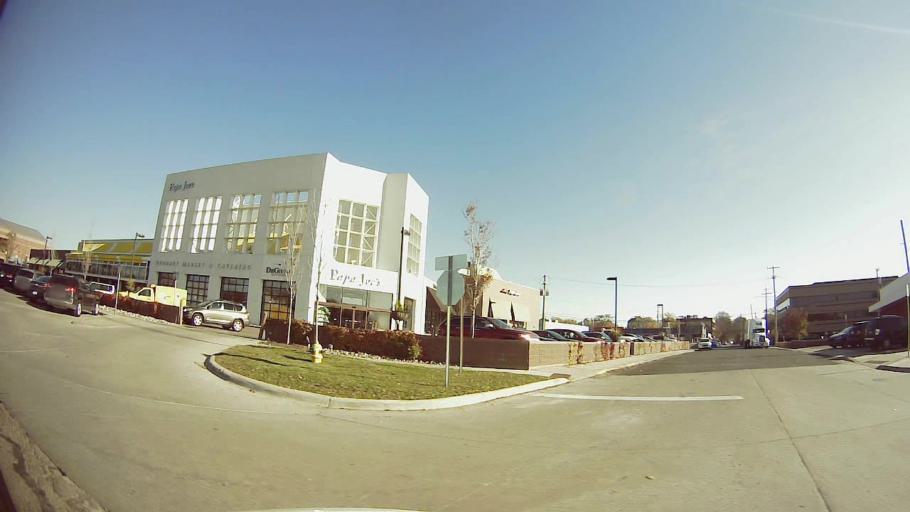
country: US
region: Michigan
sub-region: Oakland County
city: Birmingham
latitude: 42.5406
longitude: -83.2075
